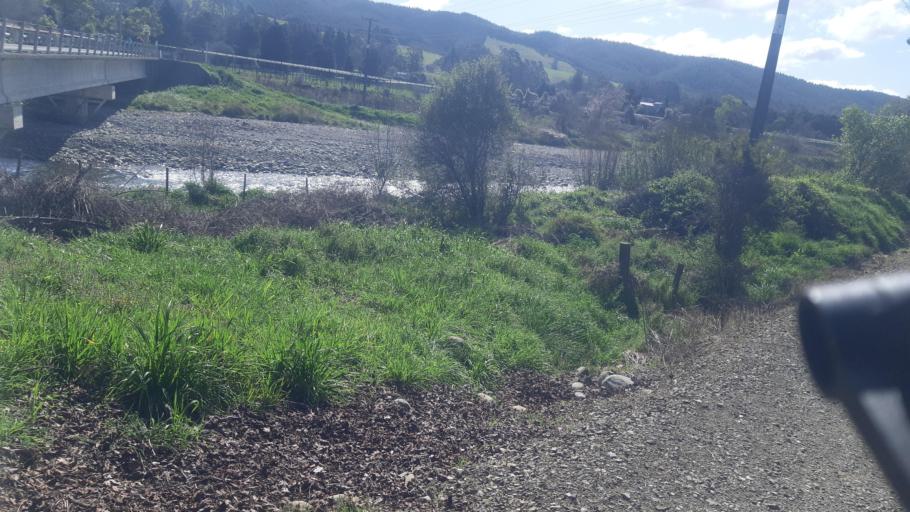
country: NZ
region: Tasman
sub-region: Tasman District
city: Wakefield
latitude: -41.4487
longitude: 172.9672
